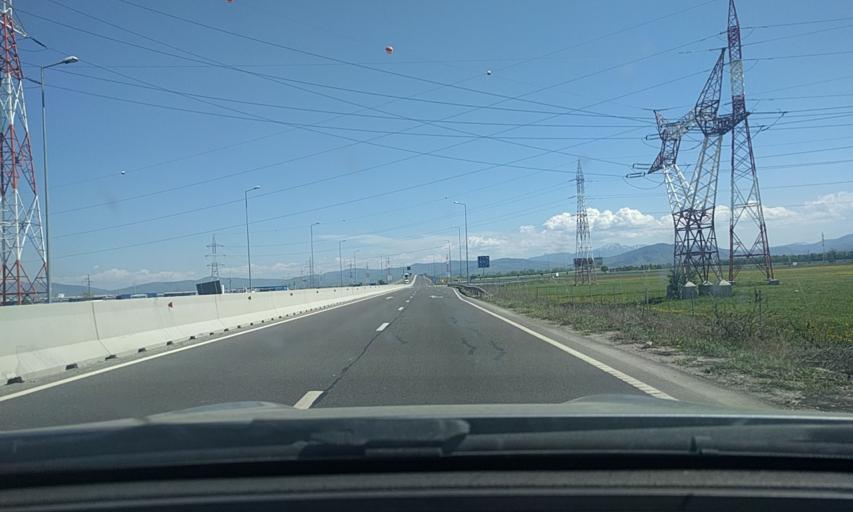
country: RO
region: Brasov
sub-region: Comuna Sanpetru
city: Sanpetru
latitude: 45.6876
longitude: 25.6555
